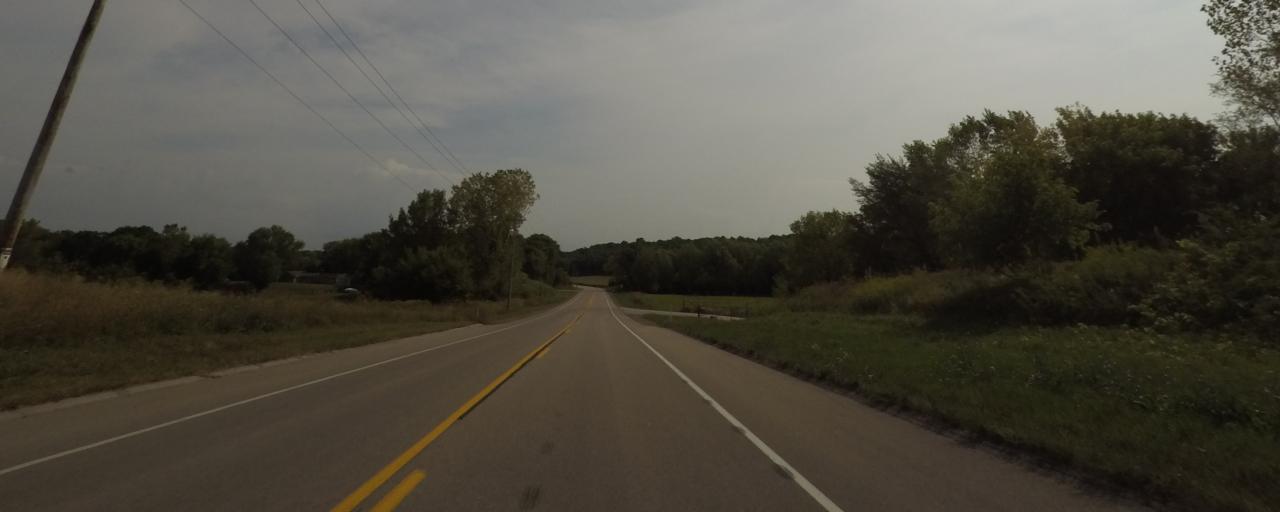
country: US
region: Wisconsin
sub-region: Jefferson County
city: Fort Atkinson
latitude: 42.9759
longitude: -88.8884
